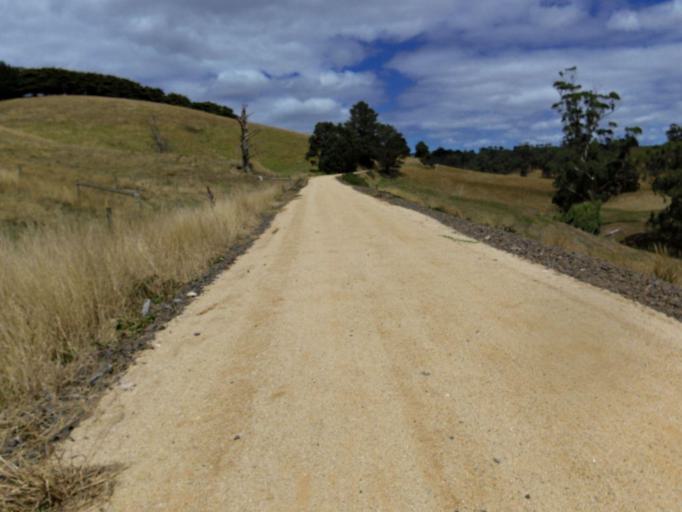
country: AU
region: Victoria
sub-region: Bass Coast
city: North Wonthaggi
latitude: -38.4084
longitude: 145.7388
